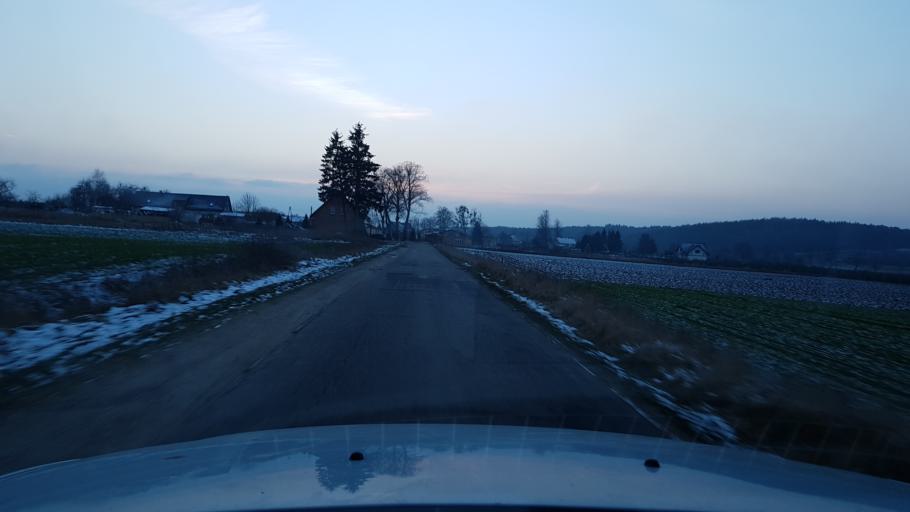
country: PL
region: West Pomeranian Voivodeship
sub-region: Powiat bialogardzki
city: Karlino
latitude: 53.9863
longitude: 15.8045
